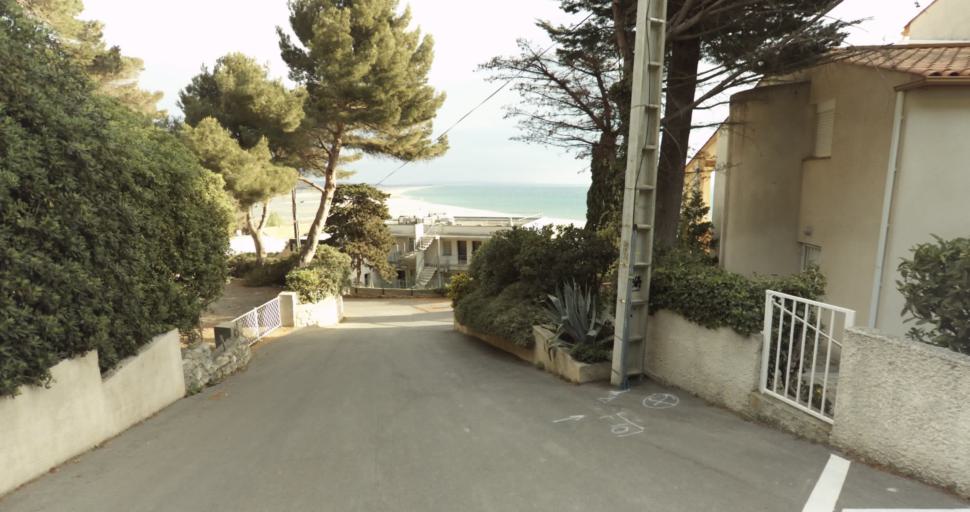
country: FR
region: Languedoc-Roussillon
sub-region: Departement de l'Aude
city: Leucate
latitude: 42.9300
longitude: 3.0384
